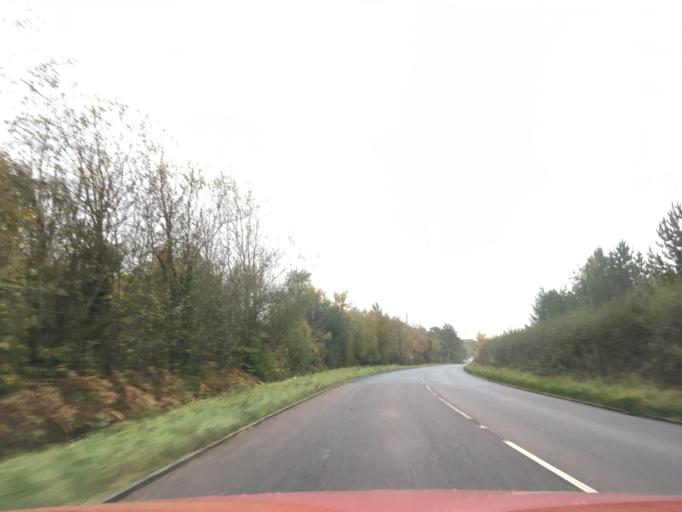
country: GB
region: England
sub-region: West Berkshire
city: Wickham
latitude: 51.4382
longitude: -1.4207
